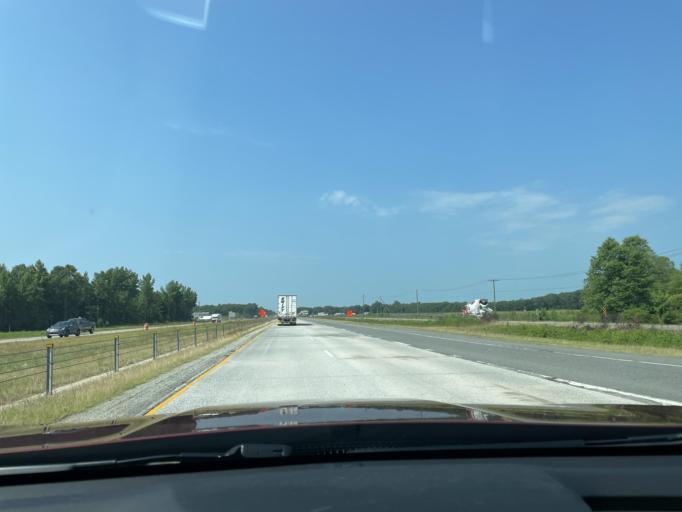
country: US
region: Arkansas
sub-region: White County
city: Searcy
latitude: 35.2017
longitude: -91.7351
